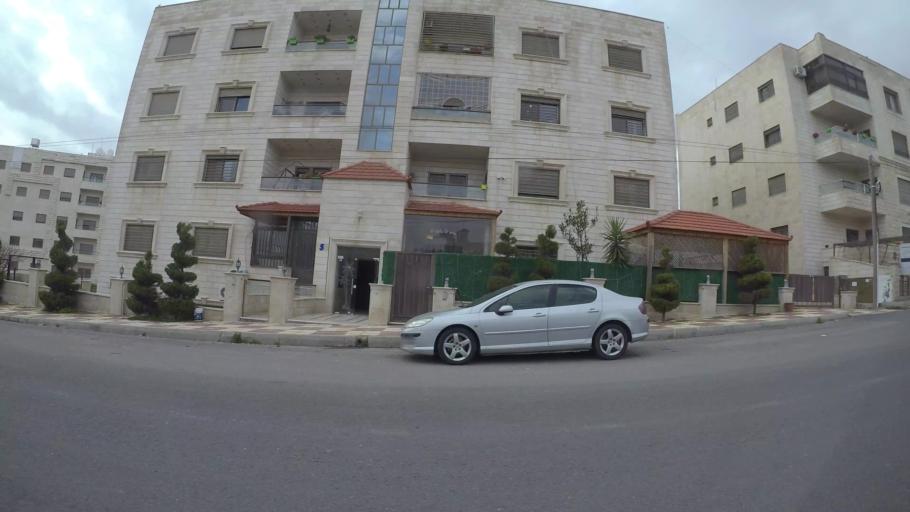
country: JO
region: Amman
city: Umm as Summaq
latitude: 31.9088
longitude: 35.8441
